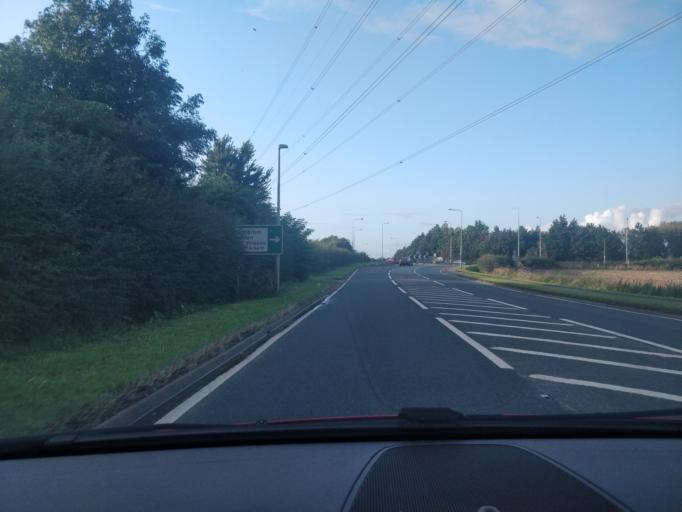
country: GB
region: England
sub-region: Lancashire
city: Tarleton
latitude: 53.6852
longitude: -2.8162
